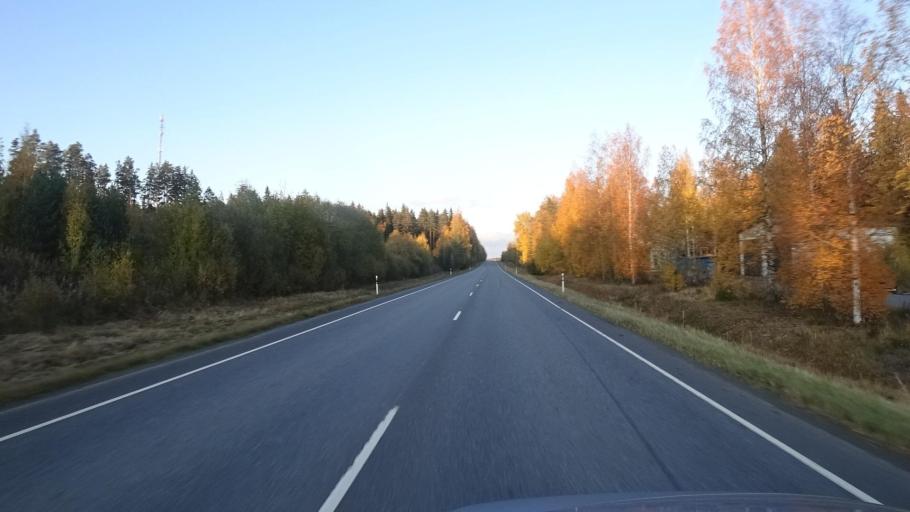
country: FI
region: Haeme
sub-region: Forssa
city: Jokioinen
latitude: 60.7945
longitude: 23.5050
